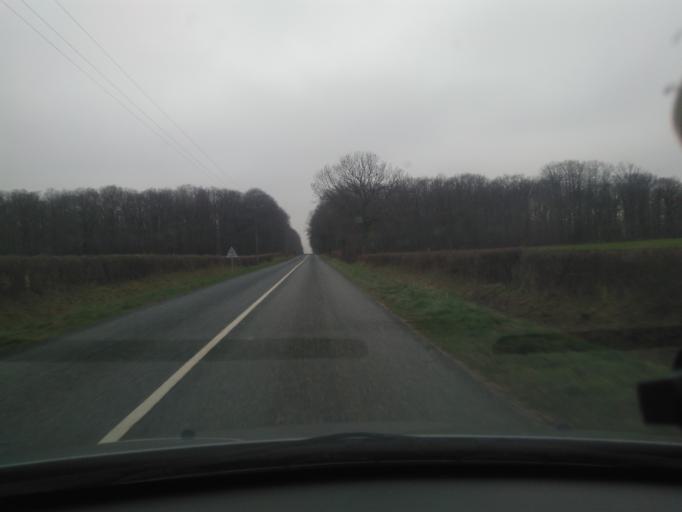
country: FR
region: Centre
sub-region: Departement du Cher
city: Chateaumeillant
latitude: 46.6366
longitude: 2.1143
